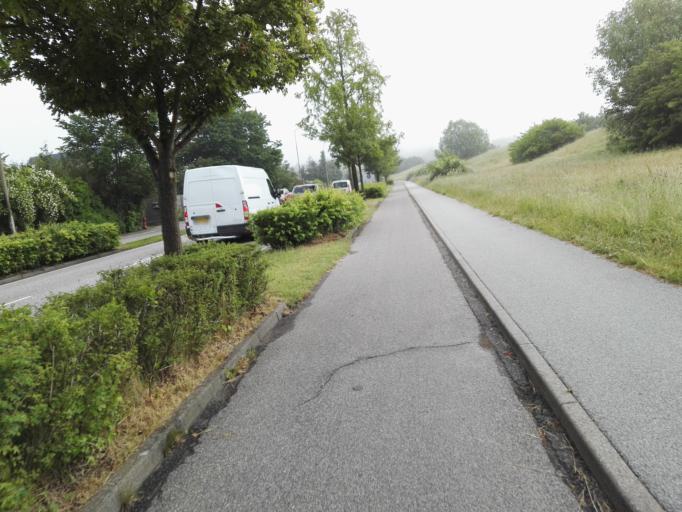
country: DK
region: Capital Region
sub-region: Ballerup Kommune
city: Ballerup
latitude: 55.7490
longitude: 12.3713
